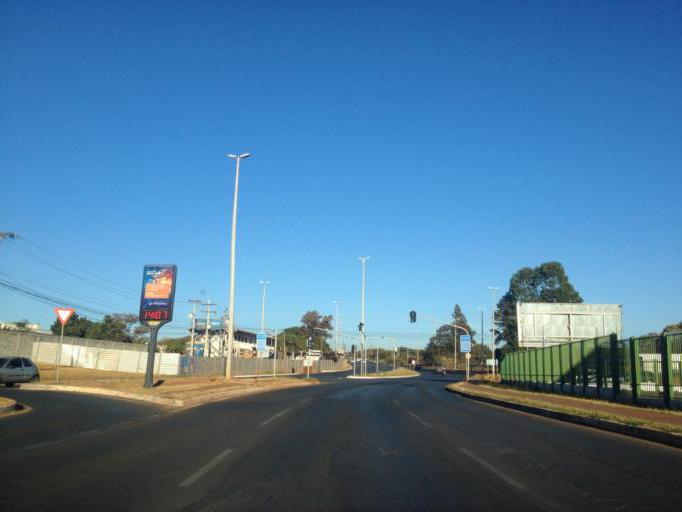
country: BR
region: Federal District
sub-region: Brasilia
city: Brasilia
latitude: -15.7697
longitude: -47.8929
